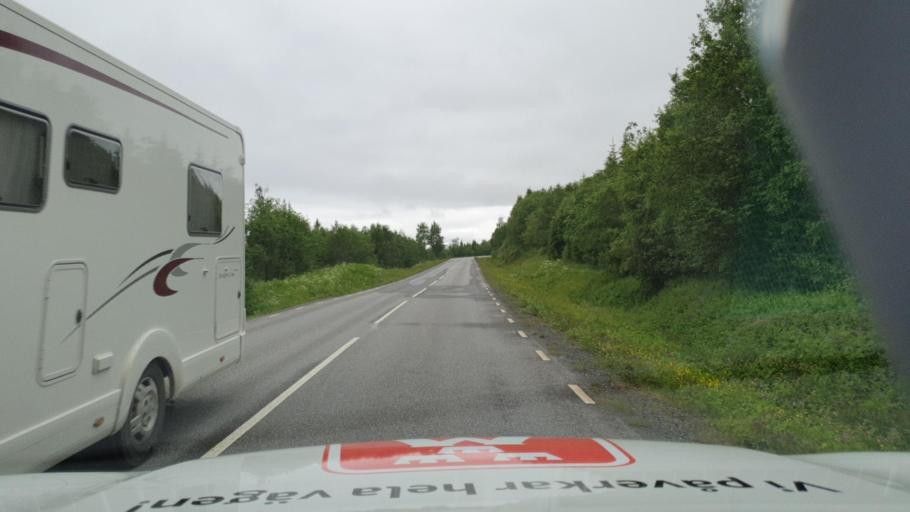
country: SE
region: Jaemtland
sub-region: Are Kommun
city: Are
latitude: 63.6273
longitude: 13.1223
